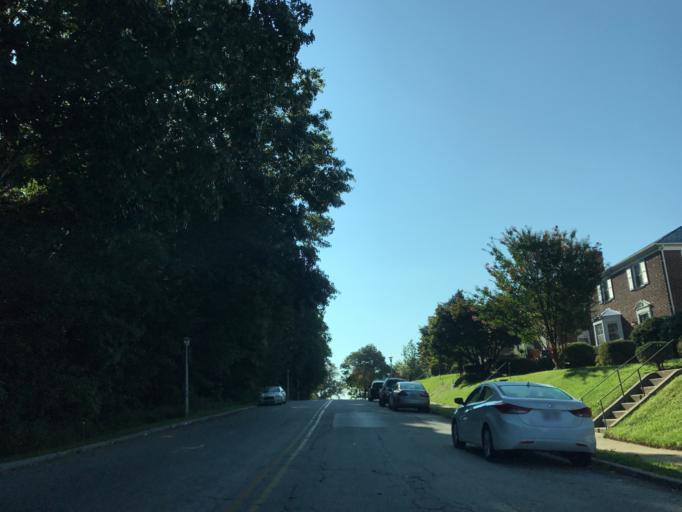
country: US
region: Maryland
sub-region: City of Baltimore
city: Baltimore
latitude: 39.3293
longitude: -76.5763
